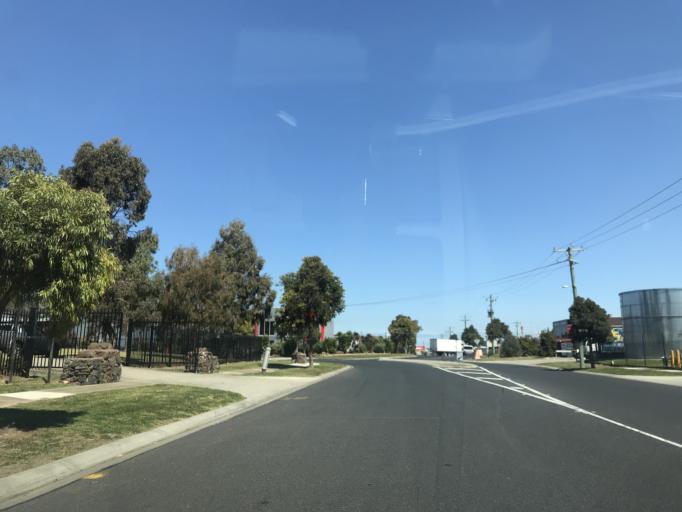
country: AU
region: Victoria
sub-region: Wyndham
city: Truganina
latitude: -37.8218
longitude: 144.7719
